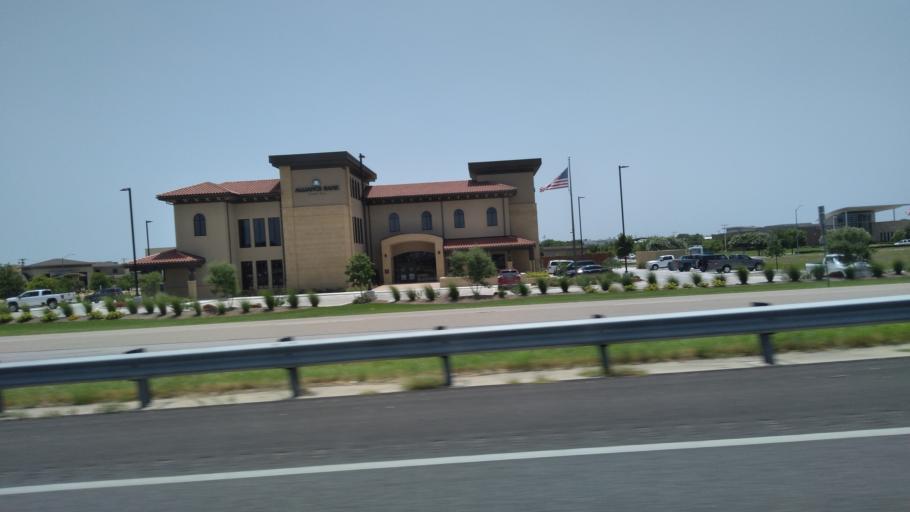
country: US
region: Texas
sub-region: McLennan County
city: Woodway
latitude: 31.5054
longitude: -97.2019
